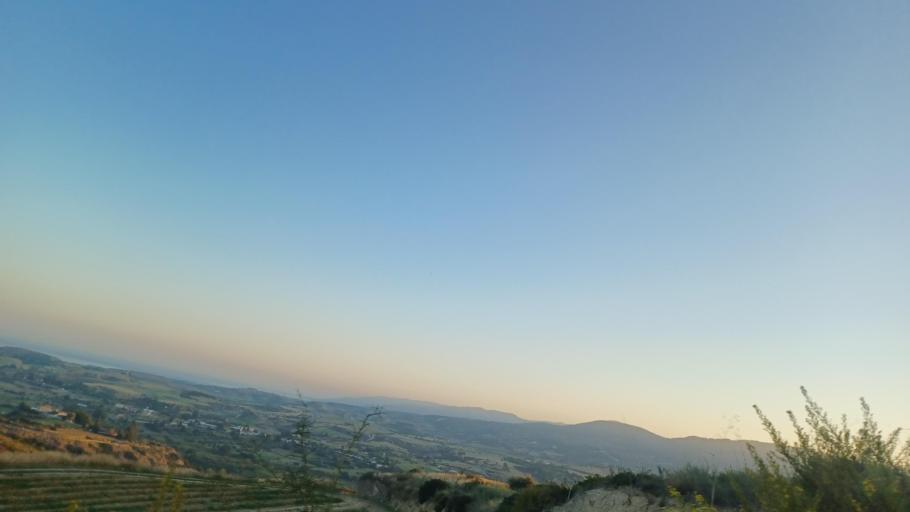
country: CY
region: Pafos
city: Polis
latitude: 34.9899
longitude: 32.4341
